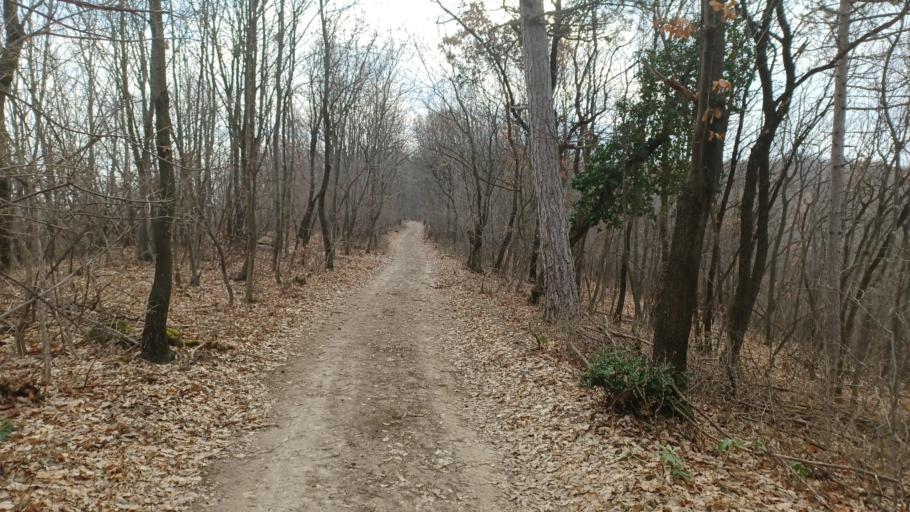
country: HU
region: Tolna
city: Szentgalpuszta
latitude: 46.3316
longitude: 18.6366
